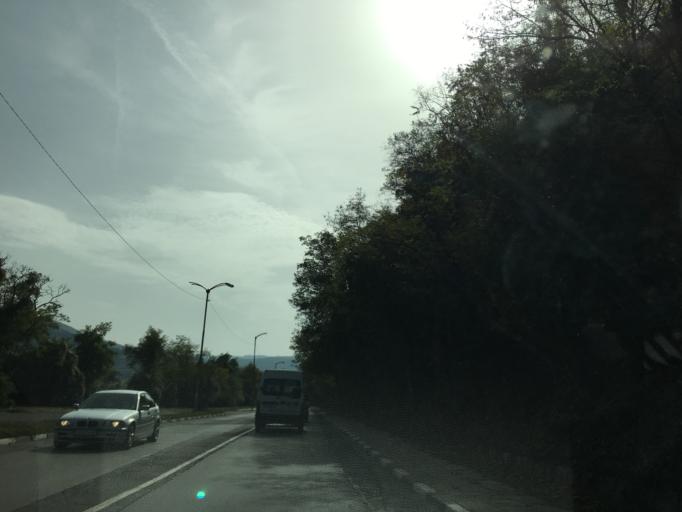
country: BG
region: Sofia-Capital
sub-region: Stolichna Obshtina
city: Sofia
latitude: 42.5925
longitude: 23.4173
